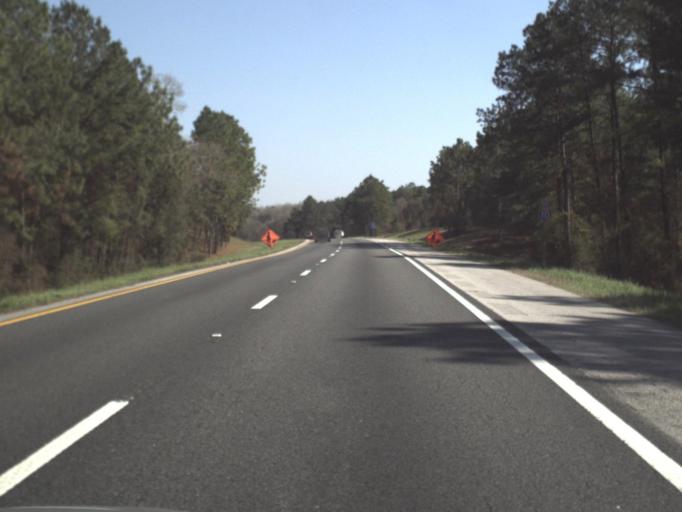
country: US
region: Florida
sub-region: Jackson County
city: Sneads
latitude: 30.6528
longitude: -85.0305
